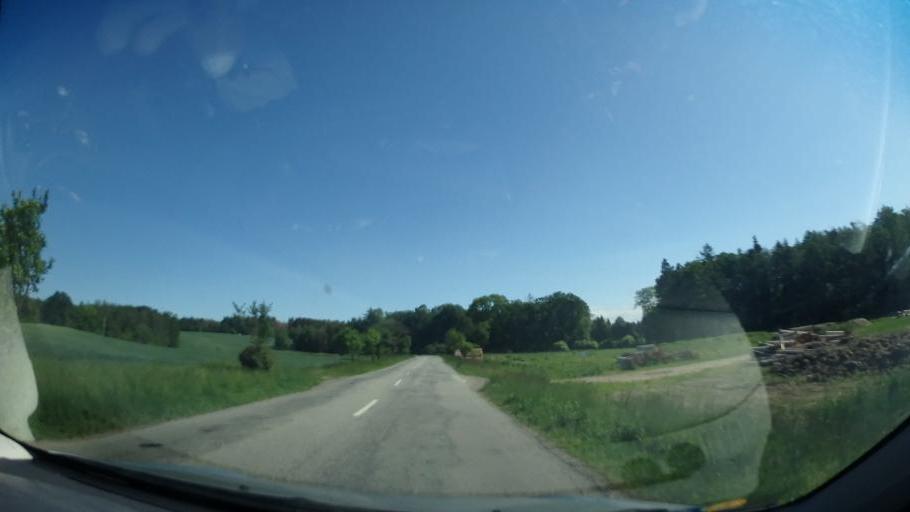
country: CZ
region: South Moravian
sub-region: Okres Blansko
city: Letovice
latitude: 49.5753
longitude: 16.5841
